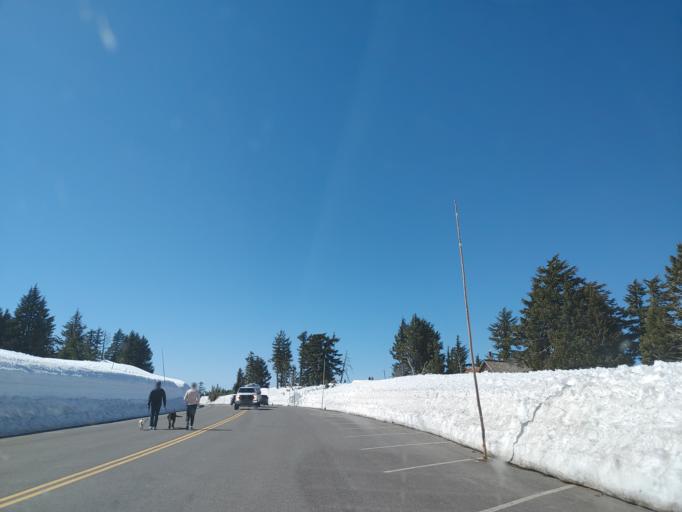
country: US
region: Oregon
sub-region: Jackson County
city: Shady Cove
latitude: 42.9105
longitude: -122.1429
